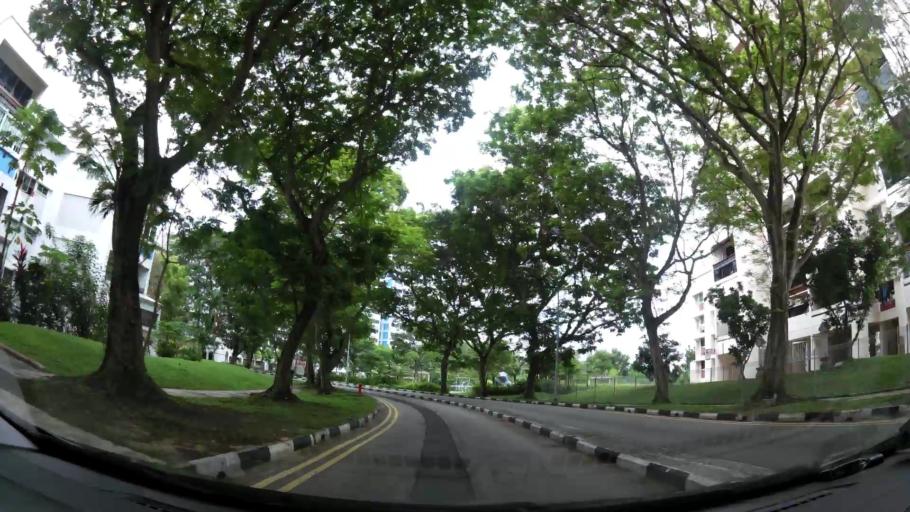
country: SG
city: Singapore
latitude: 1.3667
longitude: 103.8738
